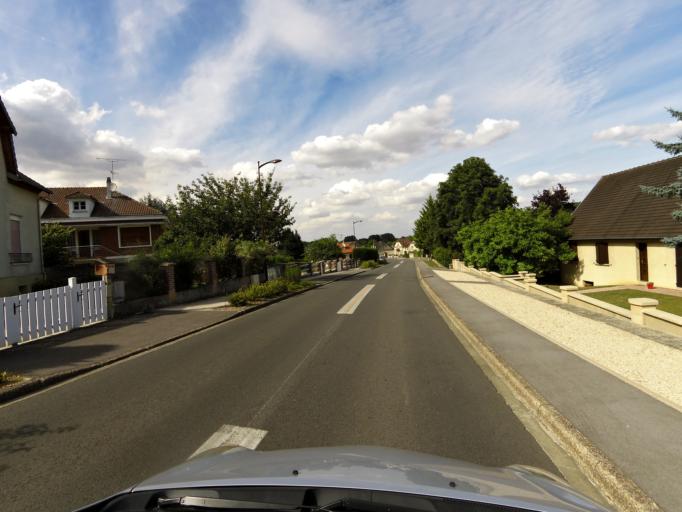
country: FR
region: Picardie
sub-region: Departement de l'Aisne
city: Bruyeres-et-Montberault
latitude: 49.5194
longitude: 3.6664
